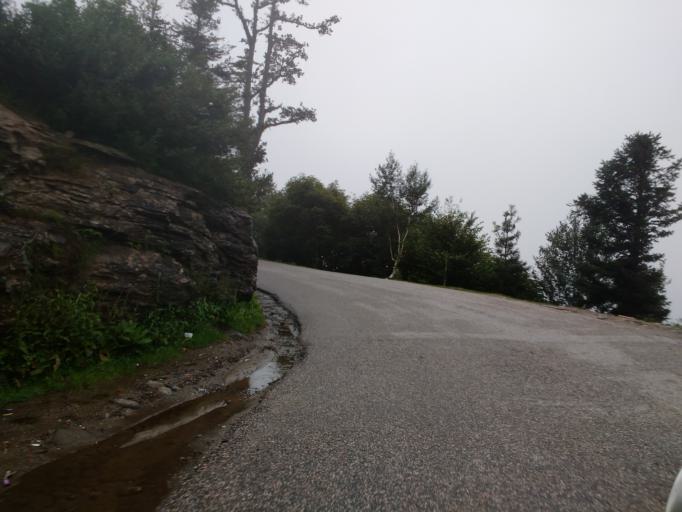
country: IN
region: Himachal Pradesh
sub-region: Kulu
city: Manali
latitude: 32.3298
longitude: 77.2025
